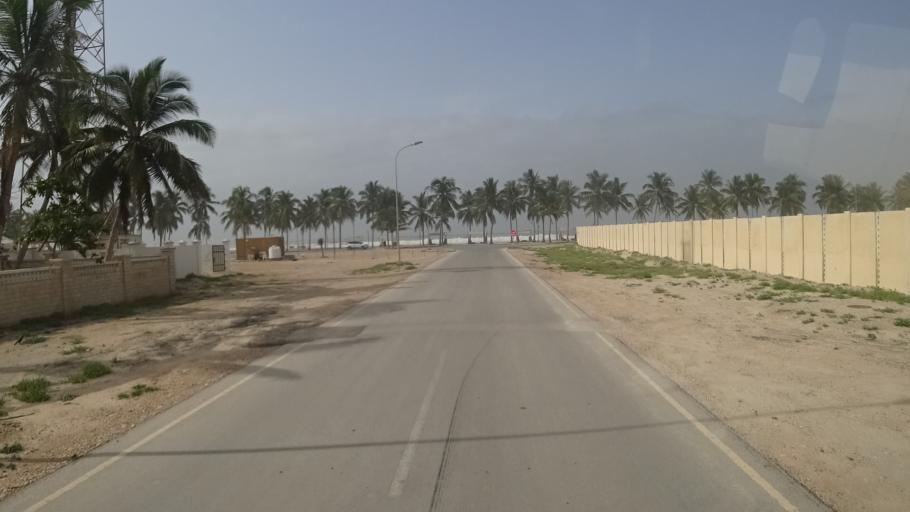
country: OM
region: Zufar
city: Salalah
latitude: 17.0119
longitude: 54.1708
